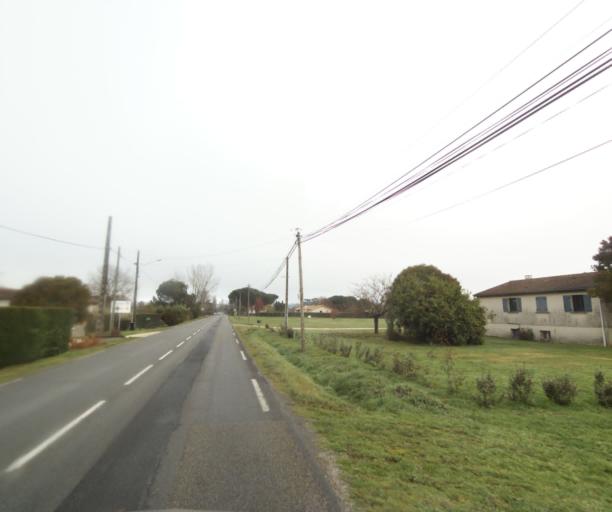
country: FR
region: Midi-Pyrenees
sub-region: Departement de la Haute-Garonne
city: Villemur-sur-Tarn
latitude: 43.8568
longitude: 1.4783
